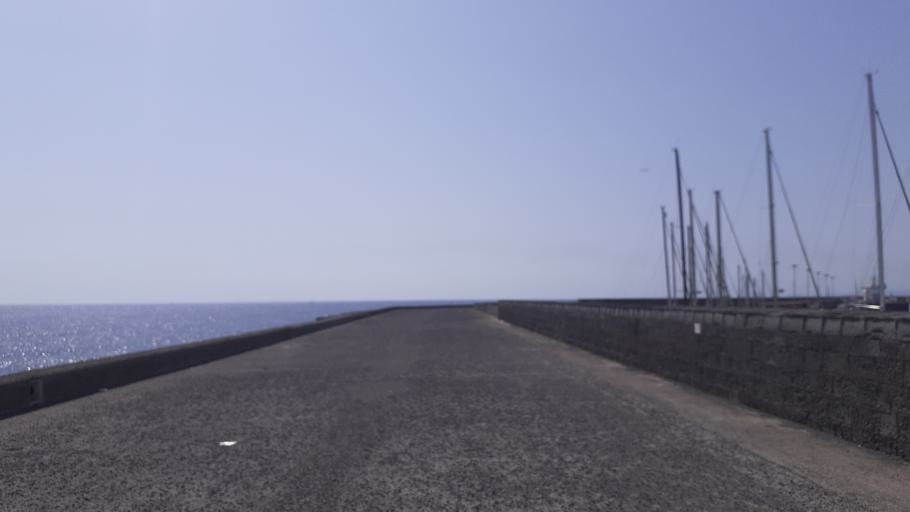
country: IT
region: Sicily
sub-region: Catania
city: Catania
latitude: 37.5010
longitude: 15.0983
